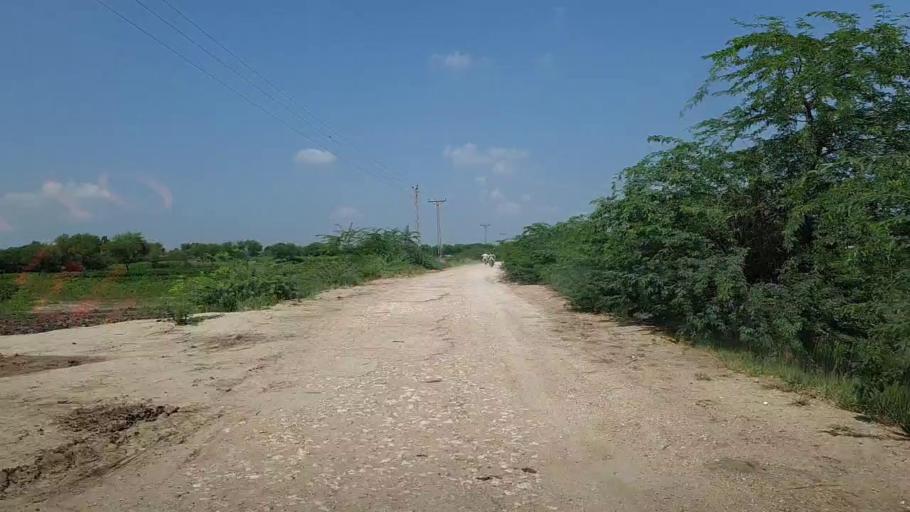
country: PK
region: Sindh
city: Kandiaro
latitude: 26.9883
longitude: 68.2467
